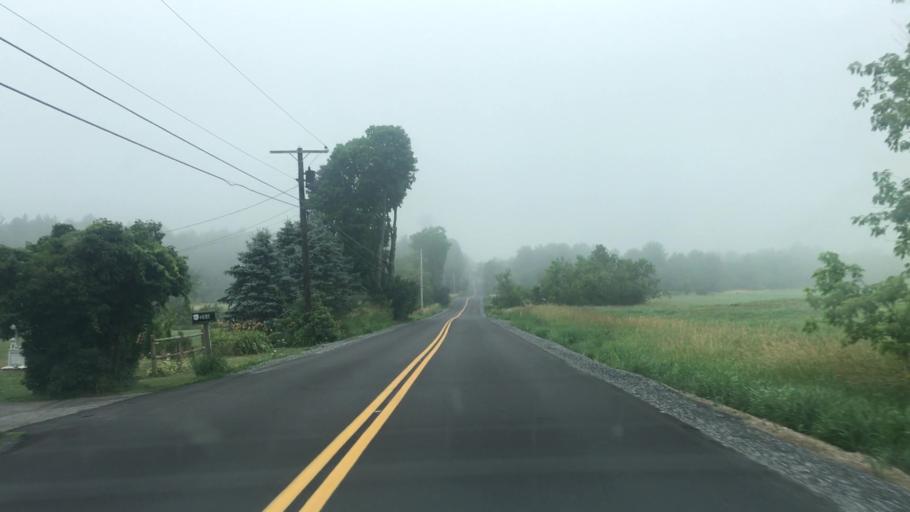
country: US
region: Maine
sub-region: Kennebec County
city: Oakland
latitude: 44.5113
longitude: -69.7093
